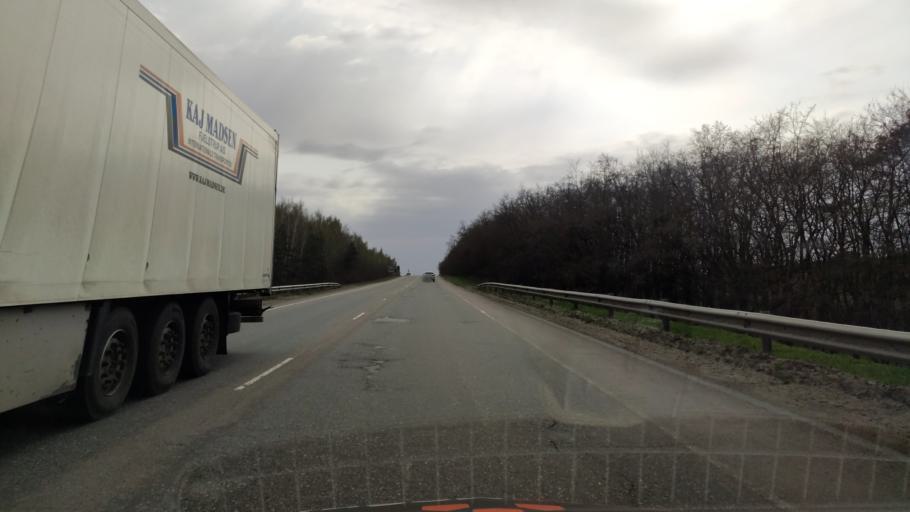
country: RU
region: Belgorod
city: Staryy Oskol
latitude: 51.4333
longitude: 37.9017
